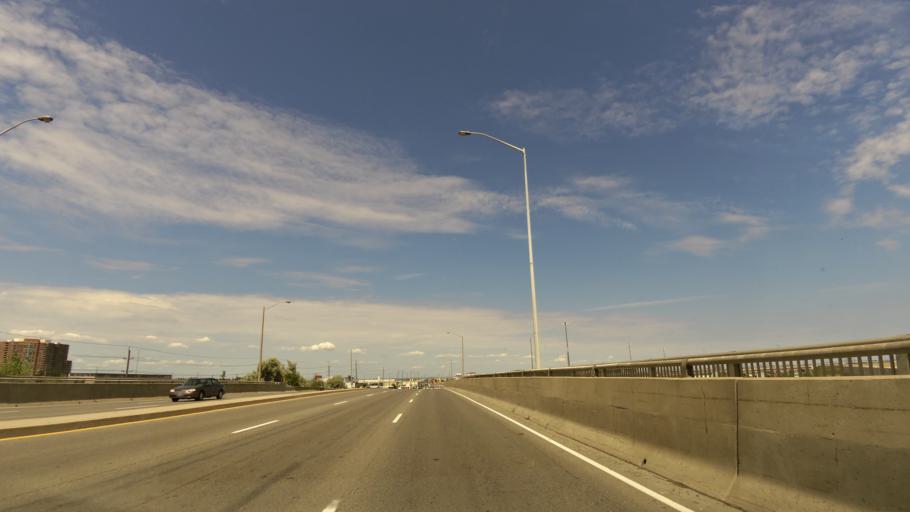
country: CA
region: Ontario
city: Brampton
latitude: 43.7006
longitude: -79.6947
